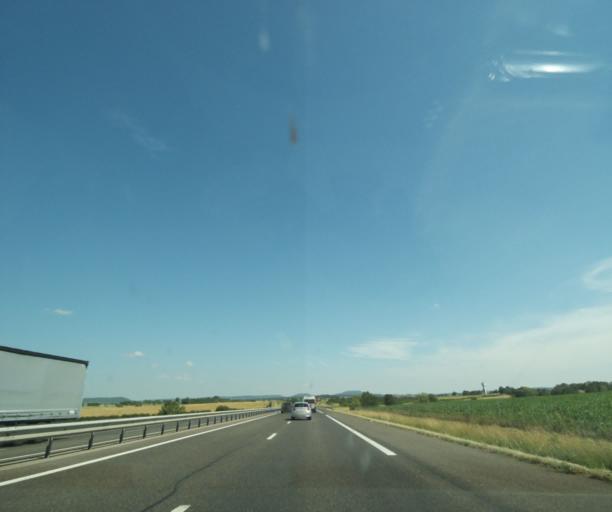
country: FR
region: Lorraine
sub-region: Departement de Meurthe-et-Moselle
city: Blenod-les-Toul
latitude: 48.5941
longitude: 5.8876
